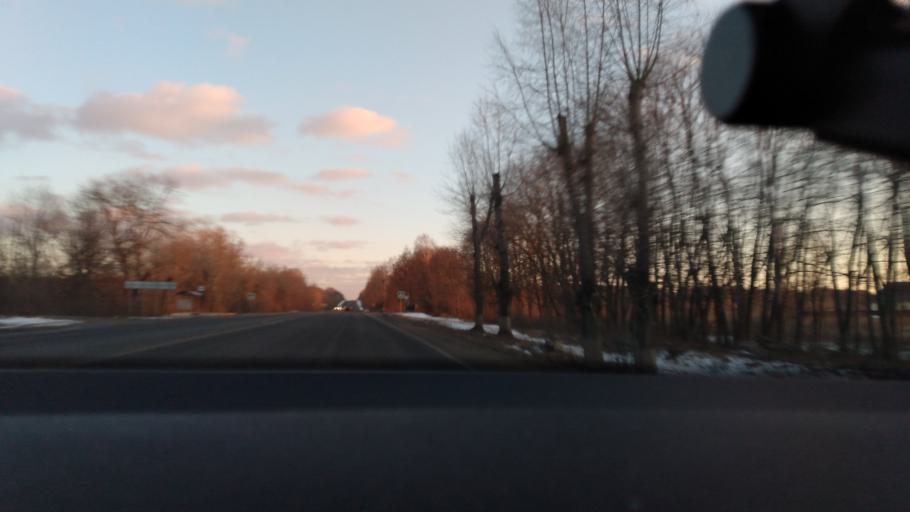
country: RU
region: Moskovskaya
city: Raduzhnyy
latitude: 55.1839
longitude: 38.6430
